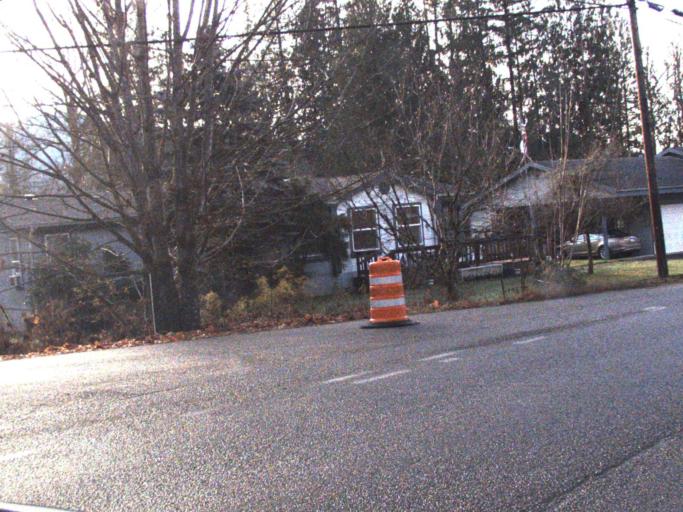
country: US
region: Washington
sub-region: Snohomish County
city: Darrington
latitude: 48.5190
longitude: -121.7070
